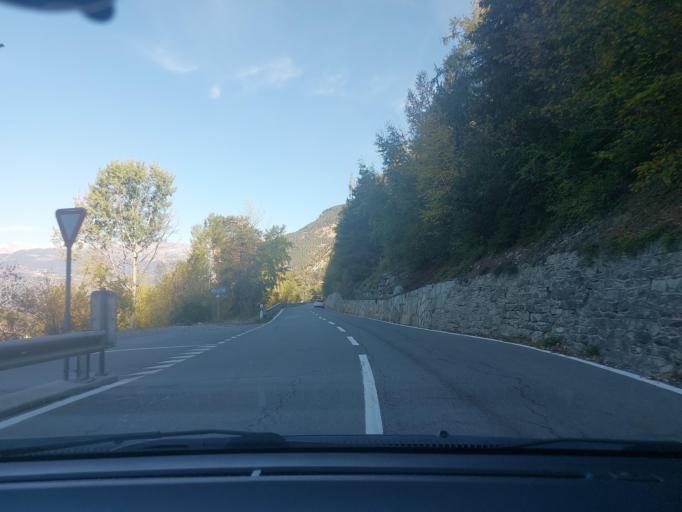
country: CH
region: Valais
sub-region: Sierre District
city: Chippis
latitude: 46.2465
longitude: 7.5757
